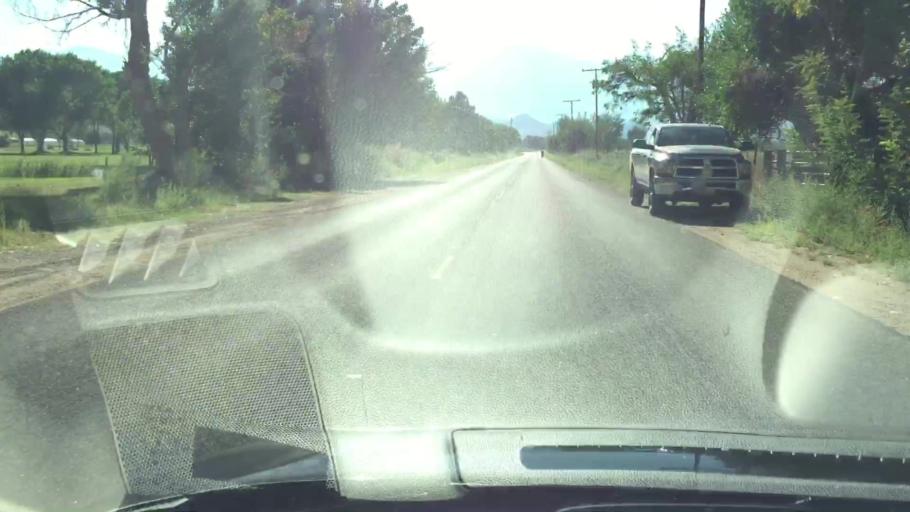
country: US
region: California
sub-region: Inyo County
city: Bishop
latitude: 37.3468
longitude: -118.3998
